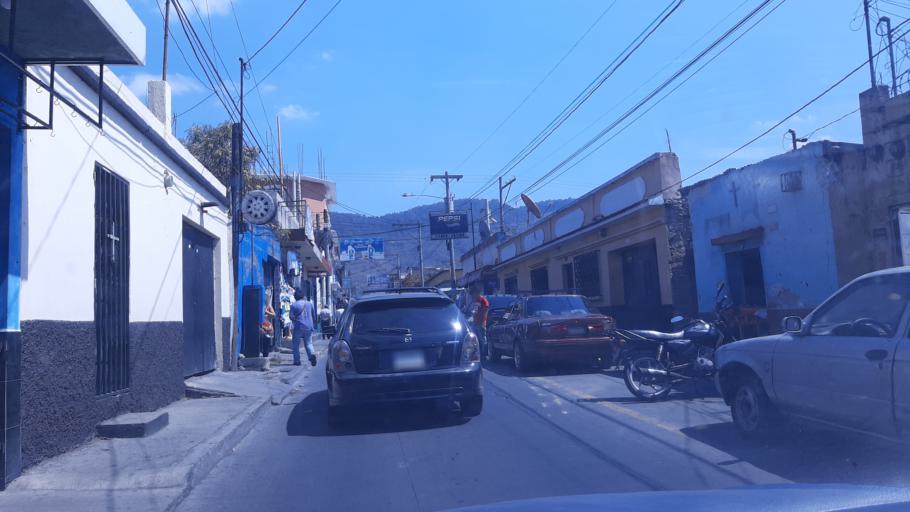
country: GT
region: Guatemala
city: Amatitlan
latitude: 14.4821
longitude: -90.6202
